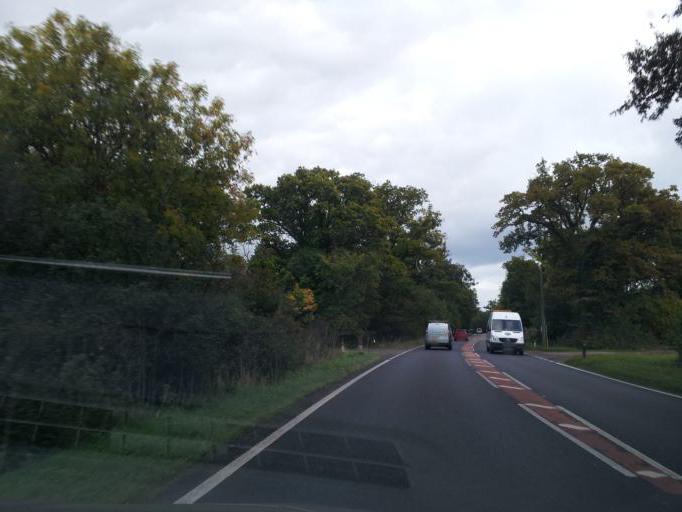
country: GB
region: England
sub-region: Cambridgeshire
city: Little Paxton
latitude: 52.2243
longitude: -0.2018
